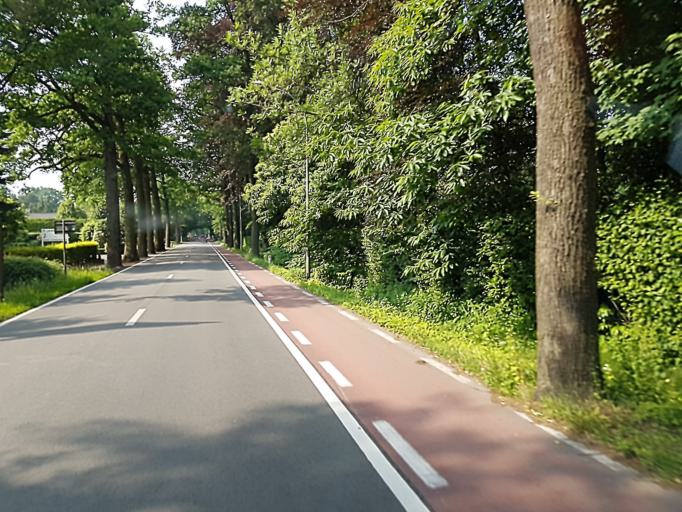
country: BE
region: Flanders
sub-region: Provincie Antwerpen
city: Turnhout
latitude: 51.3402
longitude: 4.9446
